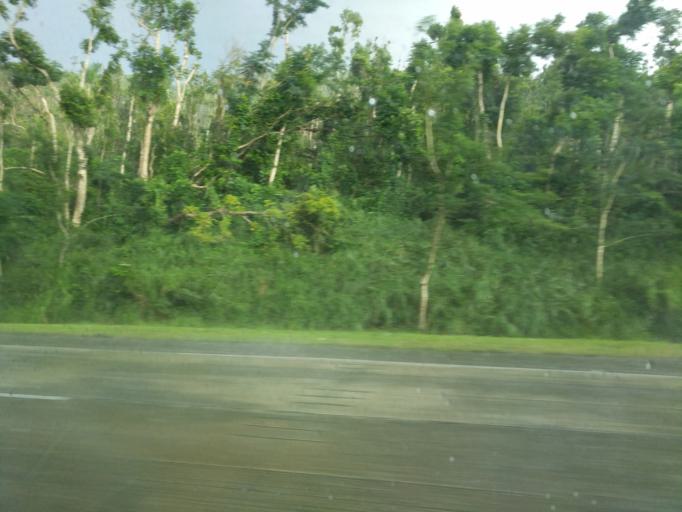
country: PR
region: Cidra
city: Bayamon
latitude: 18.1678
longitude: -66.0786
